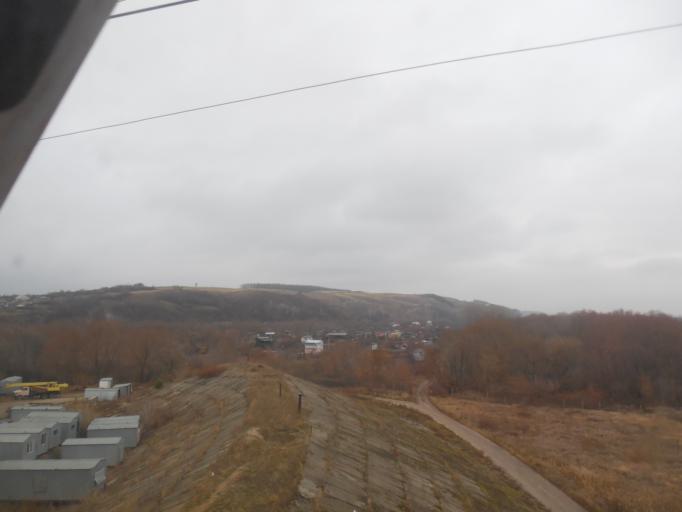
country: RU
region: Voronezj
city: Liski
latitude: 50.9632
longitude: 39.5138
